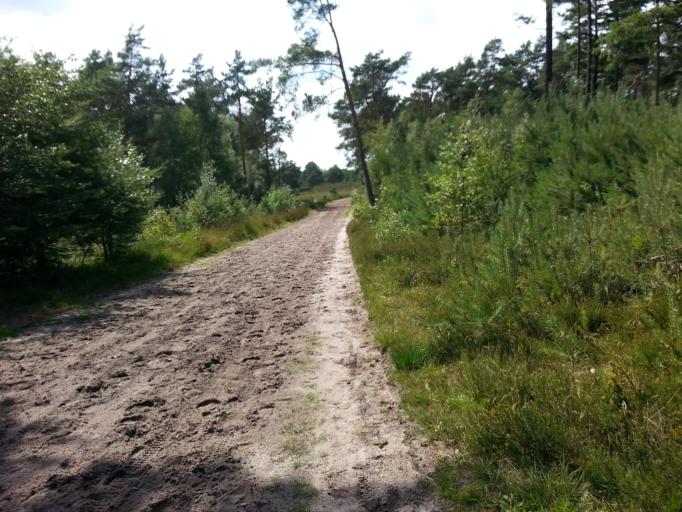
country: NL
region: Utrecht
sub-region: Gemeente Utrechtse Heuvelrug
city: Maarn
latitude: 52.0924
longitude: 5.3738
